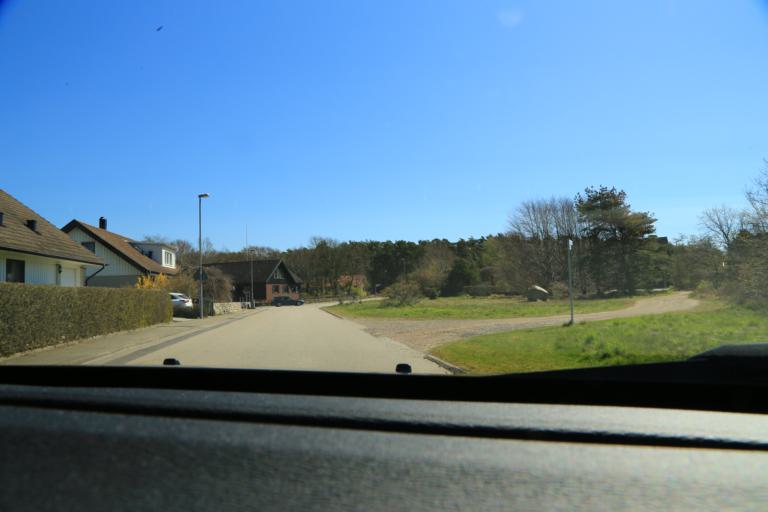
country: SE
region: Halland
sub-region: Varbergs Kommun
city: Traslovslage
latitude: 57.0498
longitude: 12.2873
